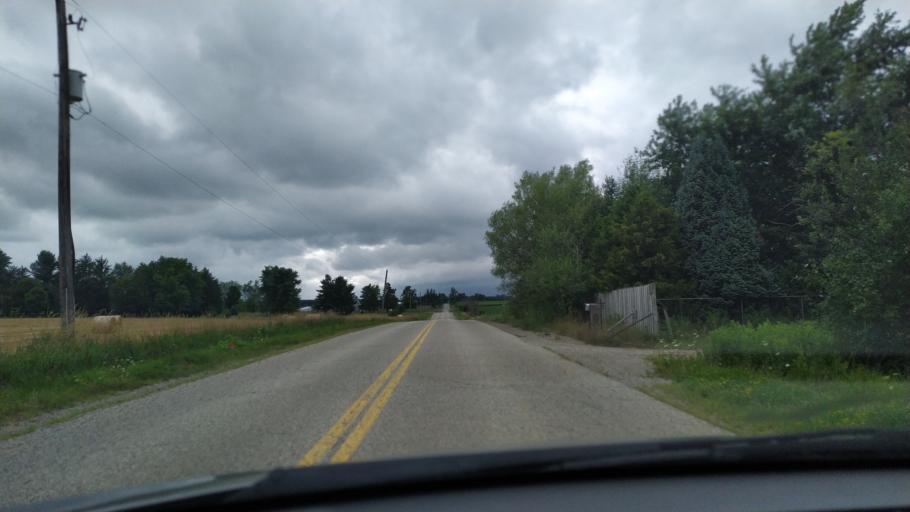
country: CA
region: Ontario
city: Kitchener
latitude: 43.3370
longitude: -80.6166
